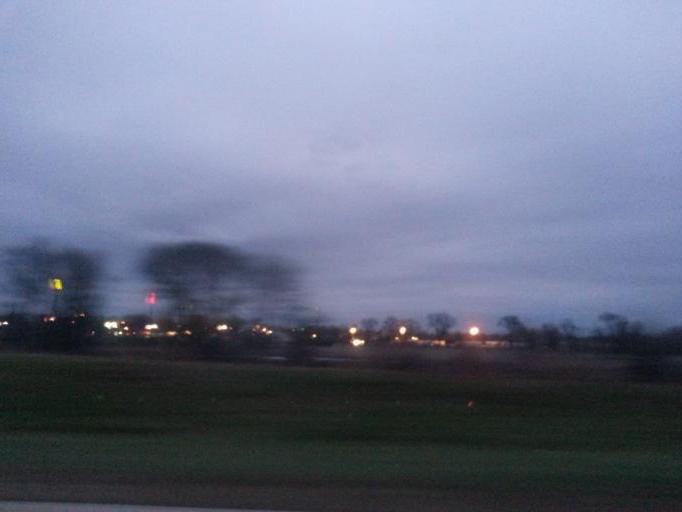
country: US
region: Iowa
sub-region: Black Hawk County
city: Elk Run Heights
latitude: 42.4565
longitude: -92.2520
